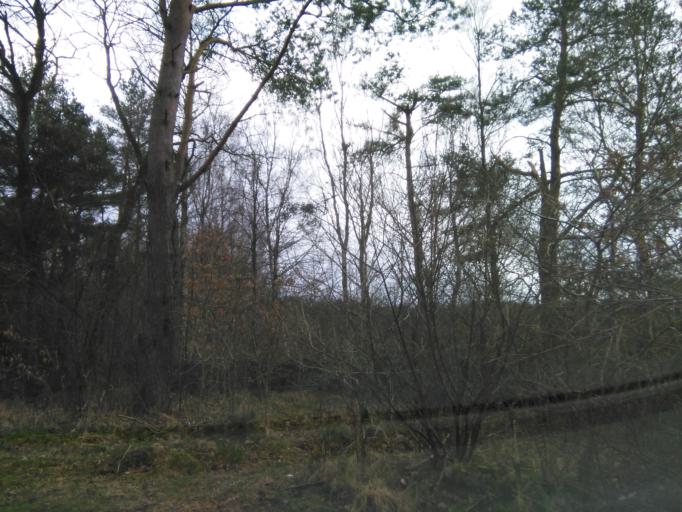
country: DK
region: Central Jutland
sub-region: Silkeborg Kommune
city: Svejbaek
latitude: 56.1184
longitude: 9.6063
